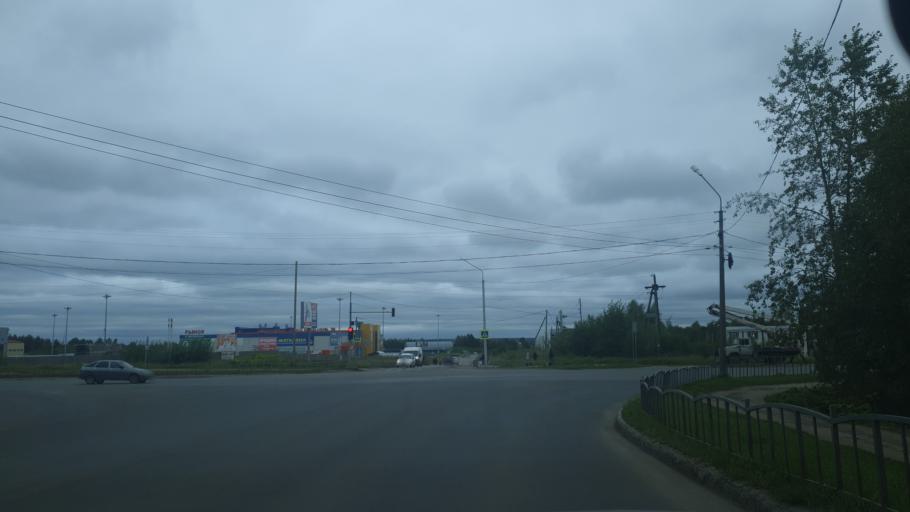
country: RU
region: Komi Republic
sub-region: Syktyvdinskiy Rayon
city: Syktyvkar
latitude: 61.6398
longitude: 50.8145
